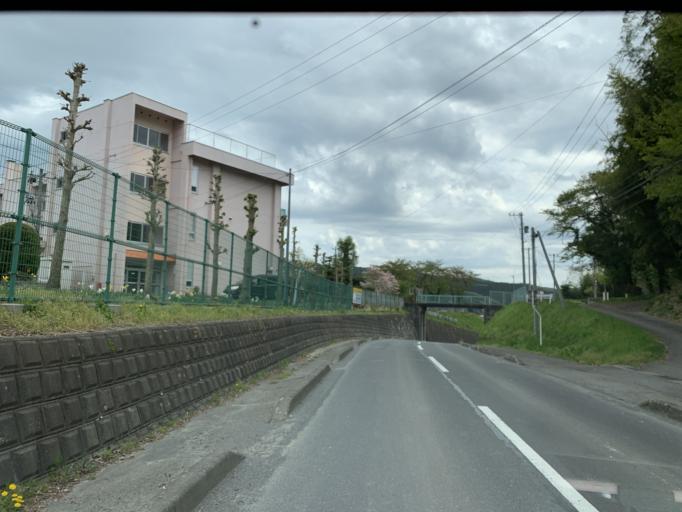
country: JP
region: Iwate
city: Ichinoseki
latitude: 38.7738
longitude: 141.3304
